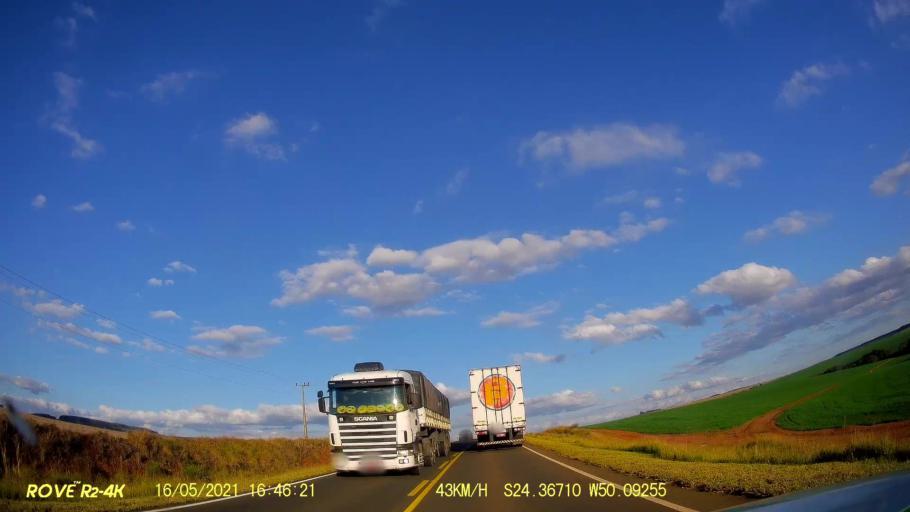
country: BR
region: Parana
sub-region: Pirai Do Sul
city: Pirai do Sul
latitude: -24.3673
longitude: -50.0919
